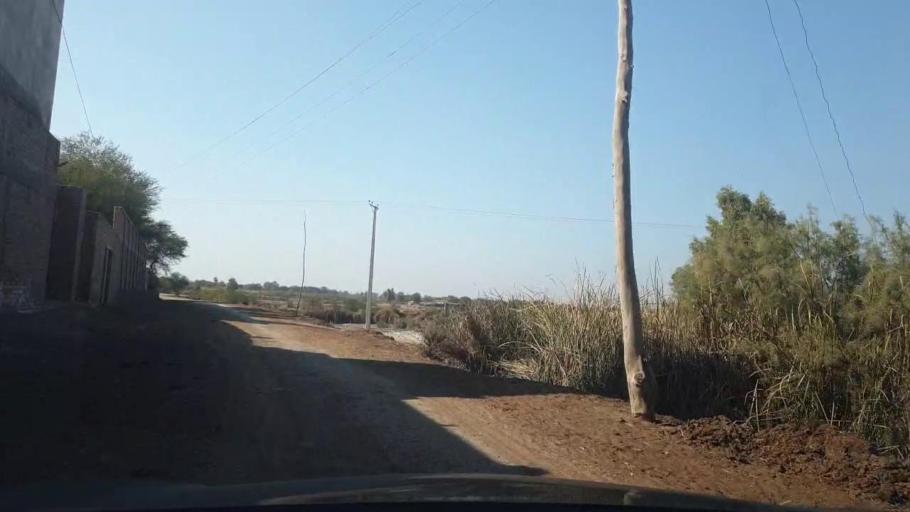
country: PK
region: Sindh
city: Khairpur
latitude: 28.1439
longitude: 69.6059
